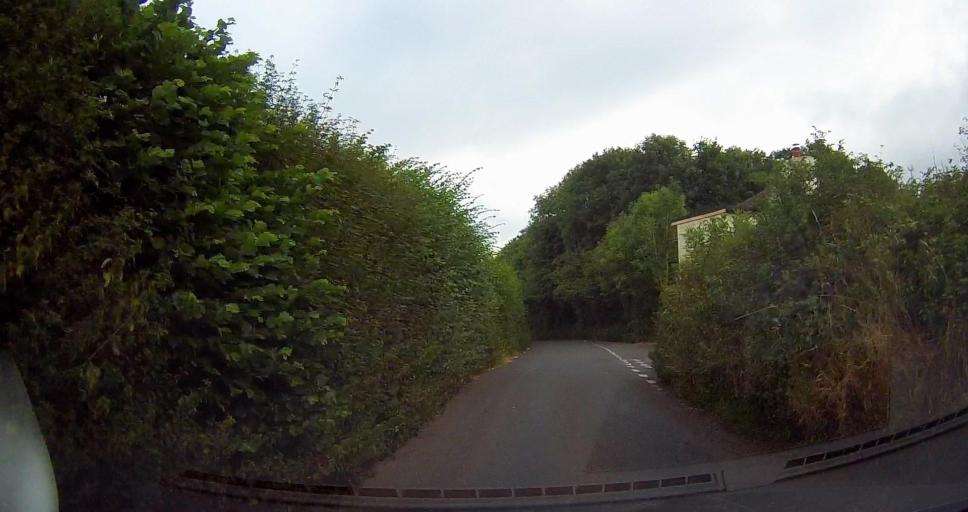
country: GB
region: England
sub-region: Devon
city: Marldon
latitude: 50.4212
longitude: -3.6016
